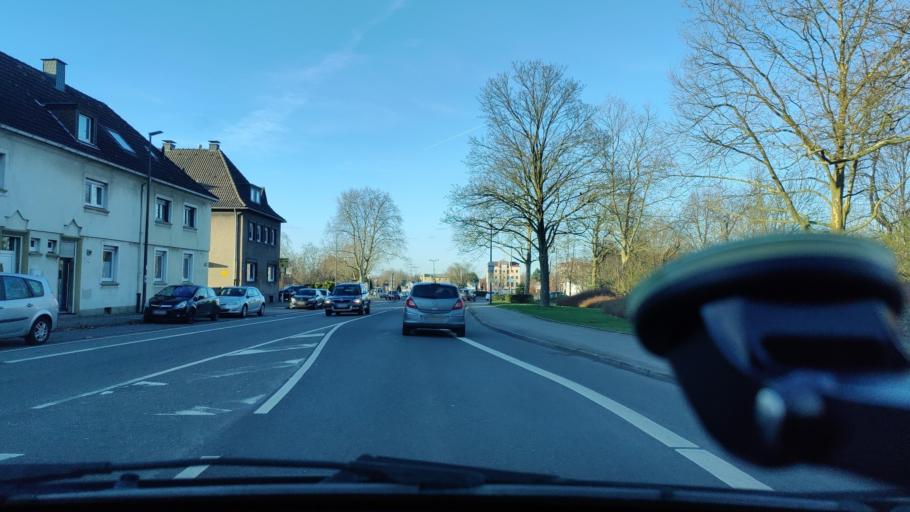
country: DE
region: North Rhine-Westphalia
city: Castrop-Rauxel
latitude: 51.5631
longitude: 7.3094
